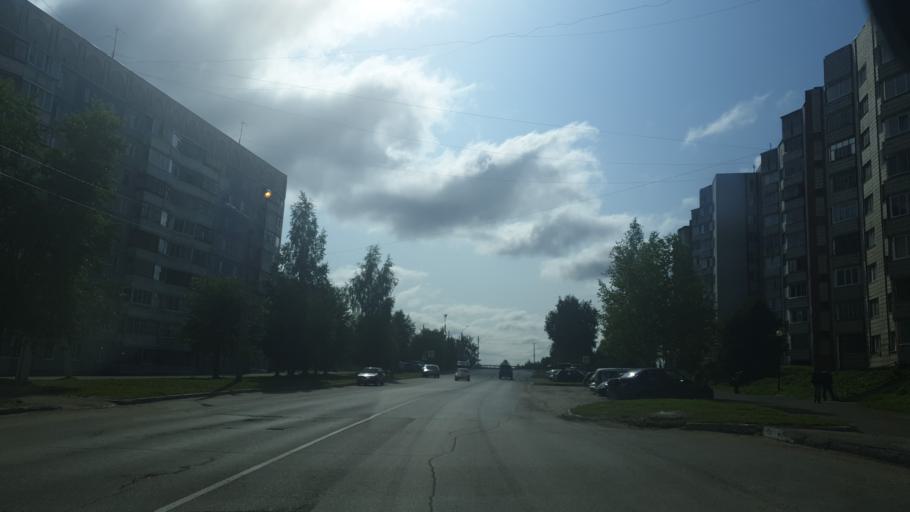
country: RU
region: Komi Republic
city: Ezhva
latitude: 61.7848
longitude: 50.7581
